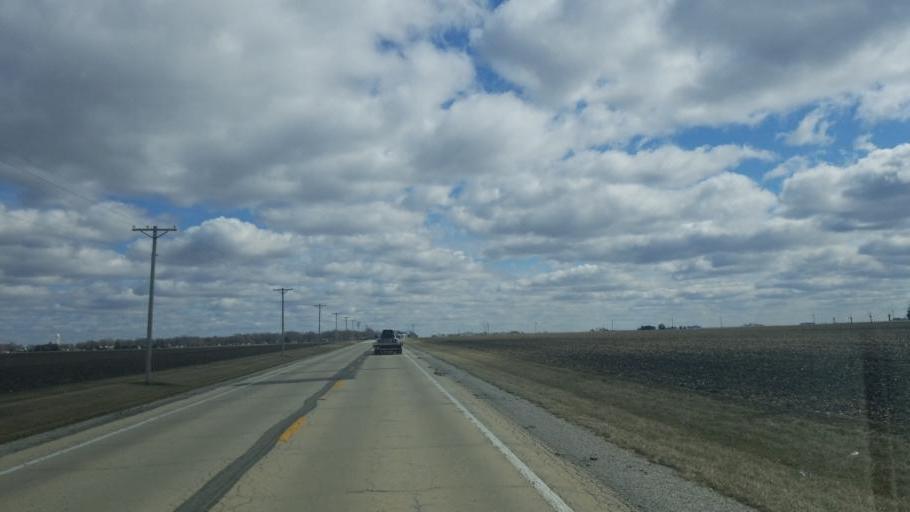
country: US
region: Illinois
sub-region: Moultrie County
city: Lovington
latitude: 39.7922
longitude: -88.6120
